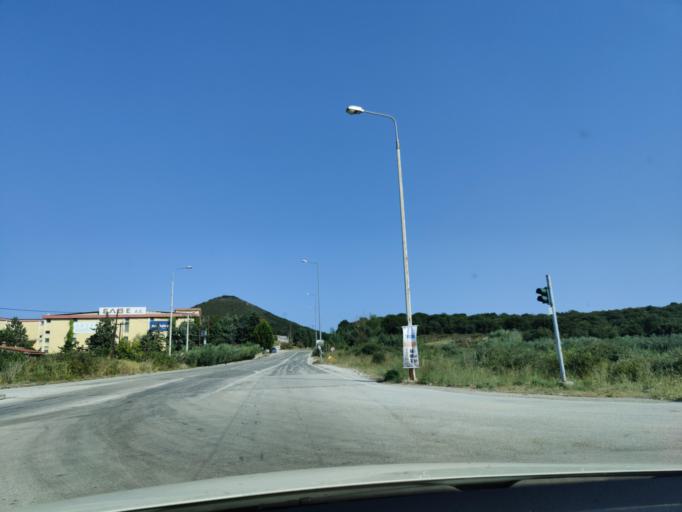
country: GR
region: East Macedonia and Thrace
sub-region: Nomos Kavalas
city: Nea Iraklitsa
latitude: 40.8656
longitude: 24.2985
